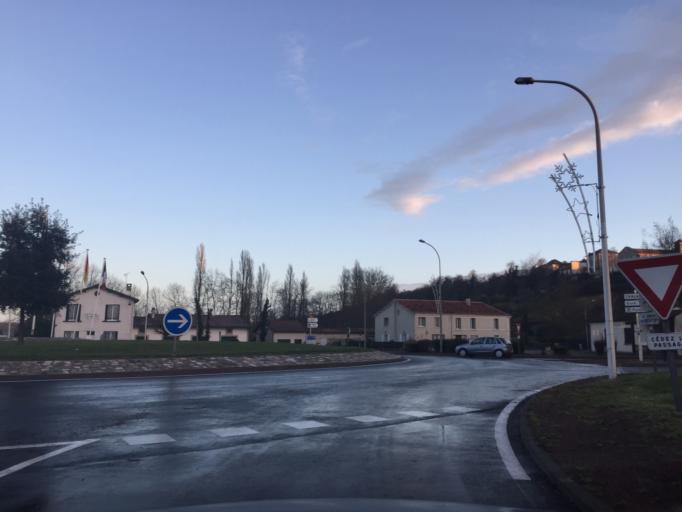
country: FR
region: Poitou-Charentes
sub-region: Departement de la Charente
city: Chalais
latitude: 45.2725
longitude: 0.0351
